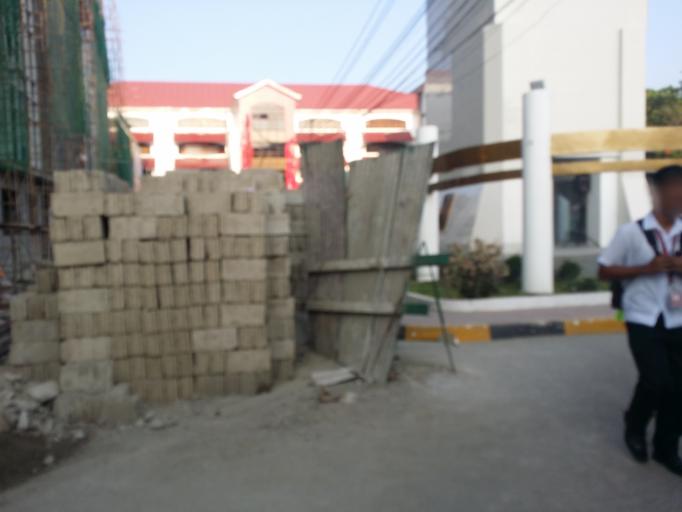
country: PH
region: Calabarzon
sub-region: Province of Batangas
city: Batangas
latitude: 13.7538
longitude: 121.0536
